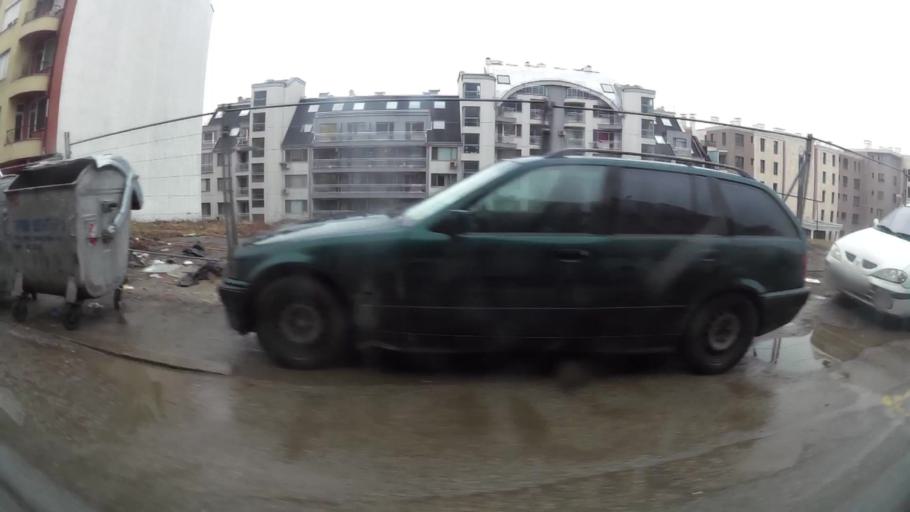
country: BG
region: Sofia-Capital
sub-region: Stolichna Obshtina
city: Sofia
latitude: 42.6401
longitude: 23.3659
